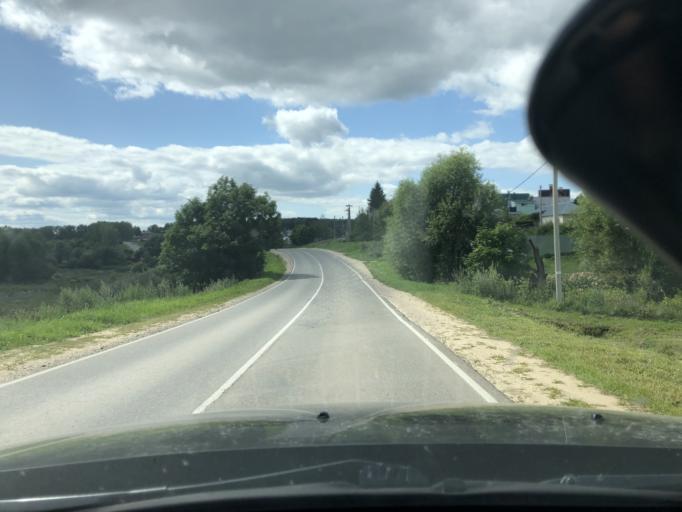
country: RU
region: Tula
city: Revyakino
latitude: 54.3628
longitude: 37.6441
